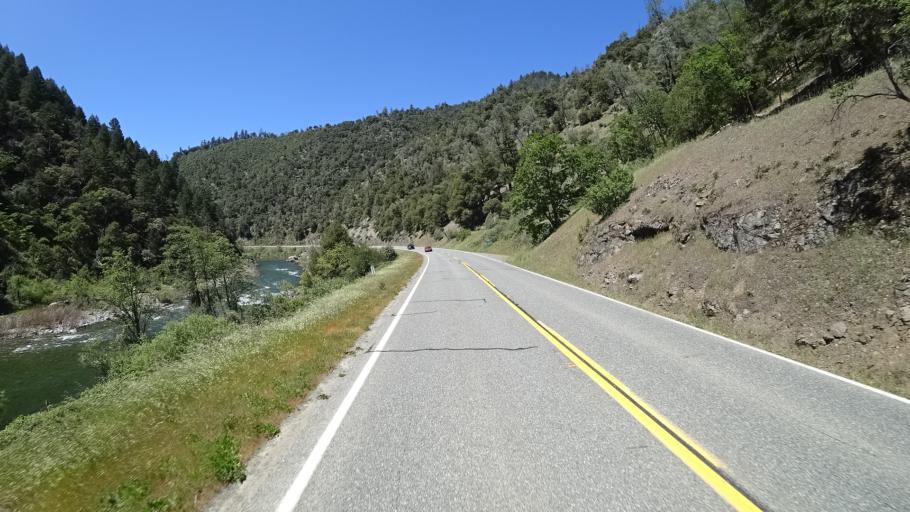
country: US
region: California
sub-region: Trinity County
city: Hayfork
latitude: 40.7656
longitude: -123.2919
